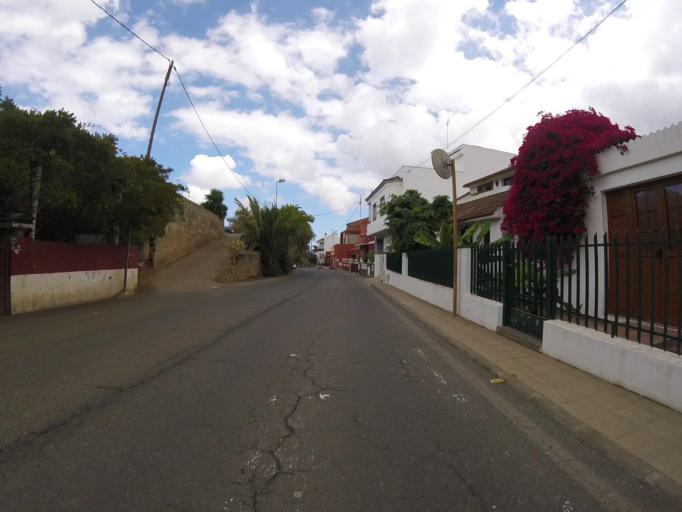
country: ES
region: Canary Islands
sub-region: Provincia de Las Palmas
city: Santa Brigida
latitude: 28.0401
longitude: -15.4913
